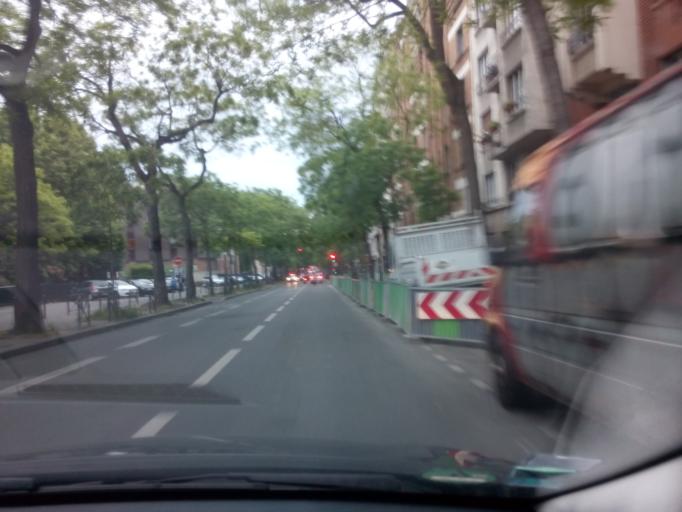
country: FR
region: Ile-de-France
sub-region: Departement du Val-de-Marne
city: Gentilly
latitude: 48.8271
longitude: 2.3373
